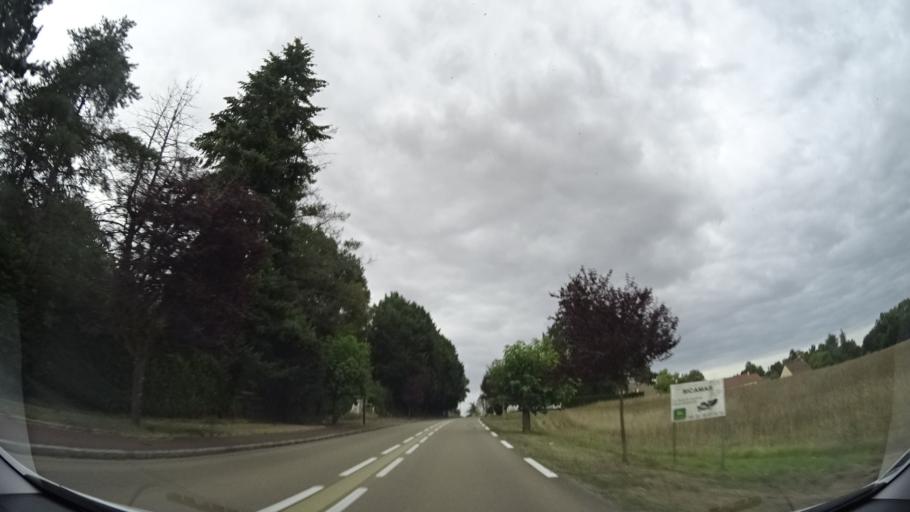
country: FR
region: Centre
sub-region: Departement du Loiret
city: Douchy
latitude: 47.9447
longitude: 3.0436
